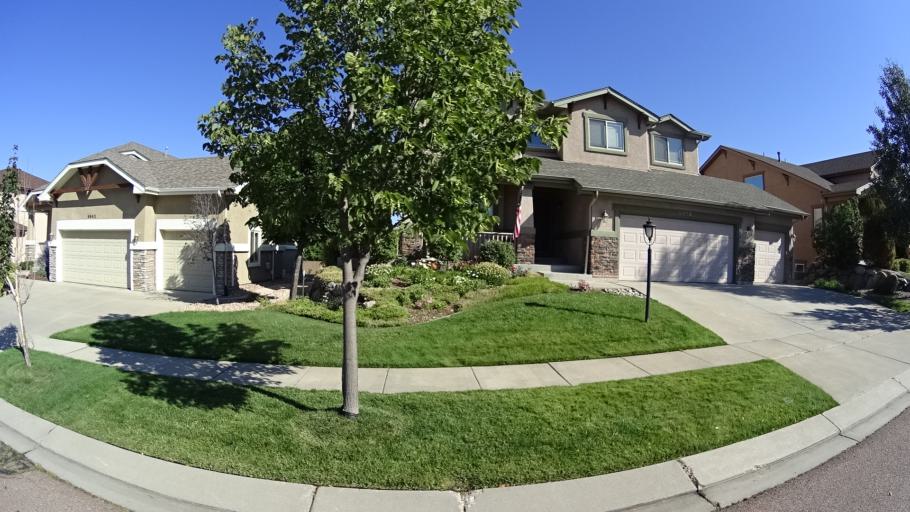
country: US
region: Colorado
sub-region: El Paso County
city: Black Forest
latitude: 38.9754
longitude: -104.7617
